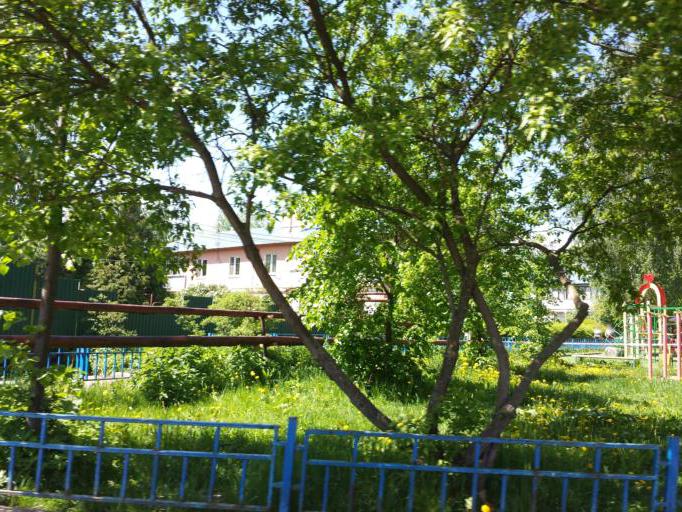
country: RU
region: Moscow
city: Lianozovo
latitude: 55.9248
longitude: 37.6110
